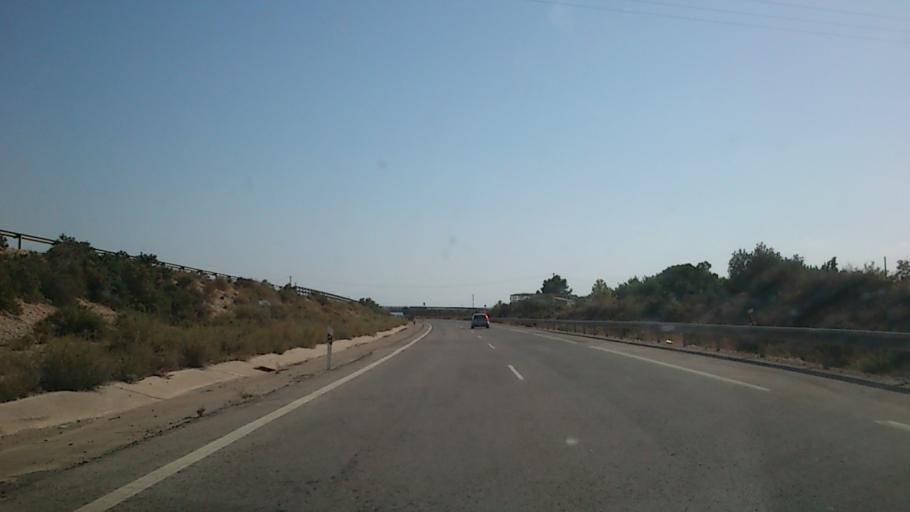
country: ES
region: Valencia
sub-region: Provincia de Alicante
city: Crevillente
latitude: 38.2169
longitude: -0.8157
